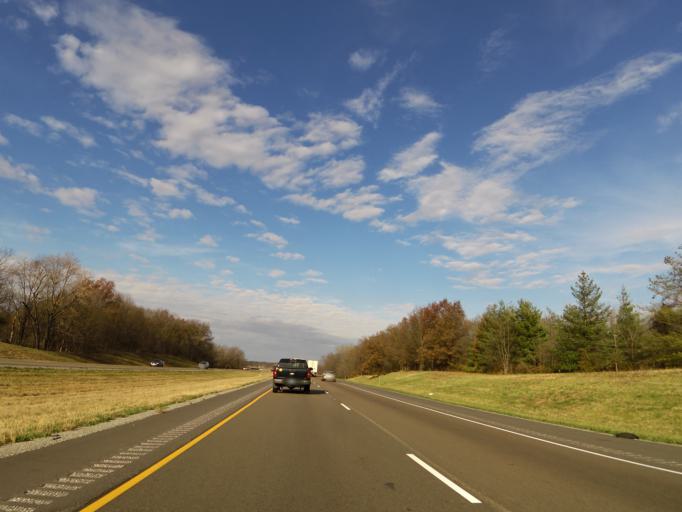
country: US
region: Illinois
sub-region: Washington County
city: Okawville
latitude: 38.4551
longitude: -89.5589
